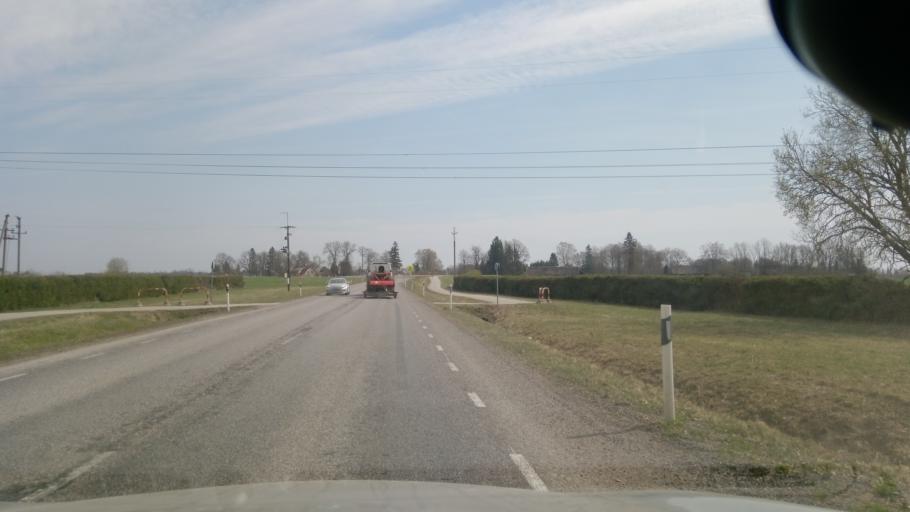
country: EE
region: Jaervamaa
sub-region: Tueri vald
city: Sarevere
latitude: 58.7792
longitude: 25.4608
